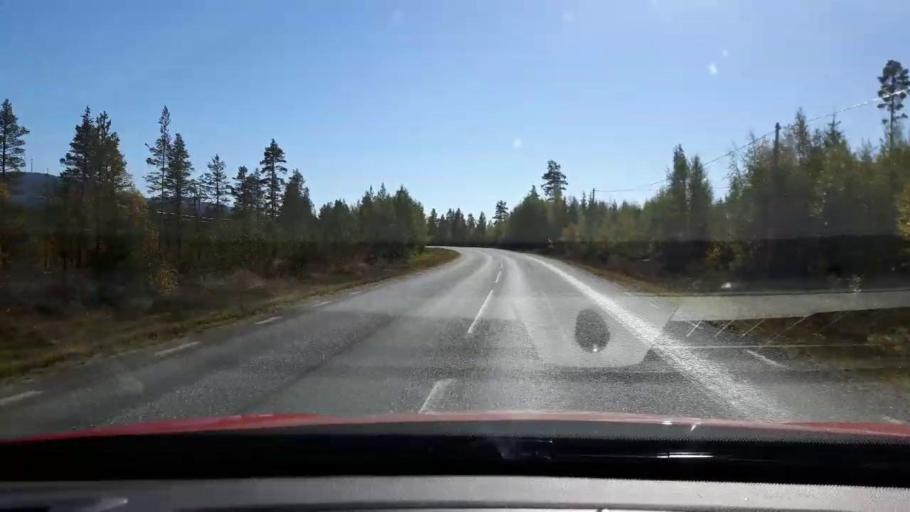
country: SE
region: Jaemtland
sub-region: Harjedalens Kommun
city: Sveg
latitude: 62.3653
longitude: 13.9939
